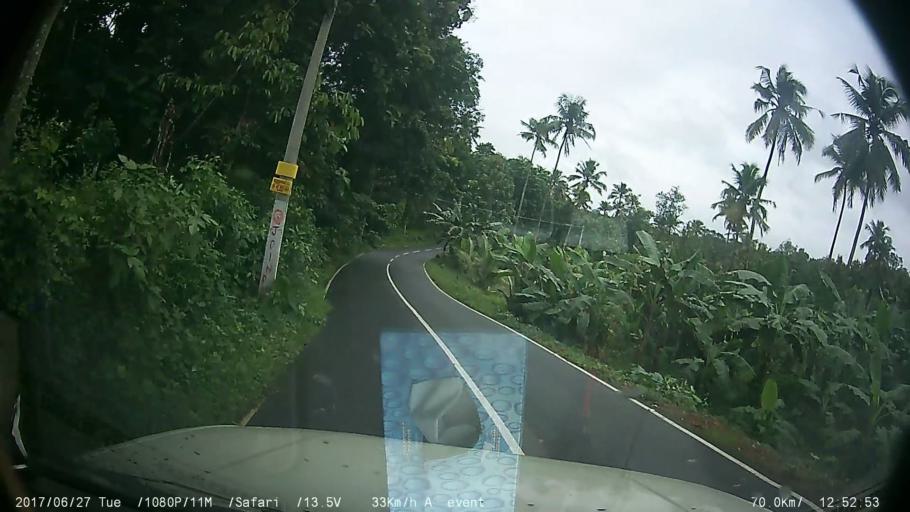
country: IN
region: Kerala
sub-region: Kottayam
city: Palackattumala
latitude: 9.7815
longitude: 76.5425
